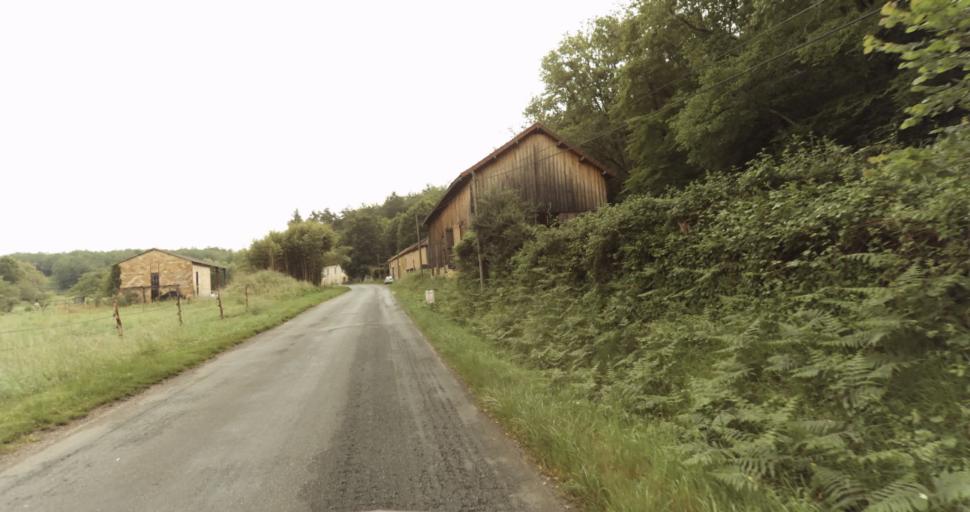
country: FR
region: Aquitaine
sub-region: Departement de la Dordogne
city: Lalinde
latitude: 44.8774
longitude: 0.7774
